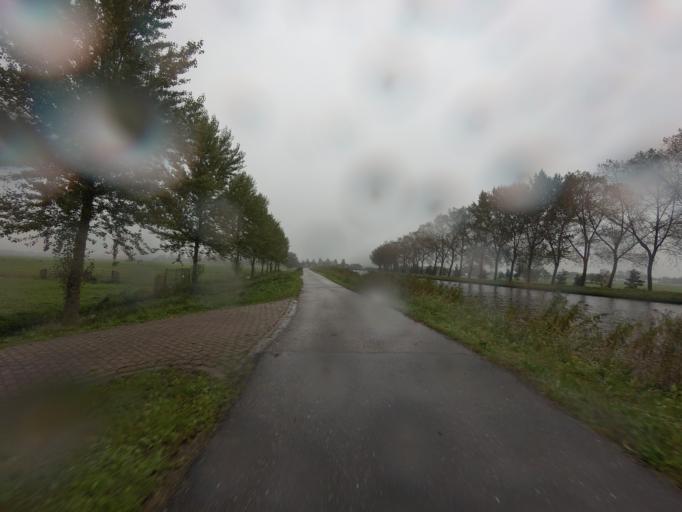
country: NL
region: South Holland
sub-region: Gemeente Leerdam
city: Leerdam
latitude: 51.9341
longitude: 5.0351
